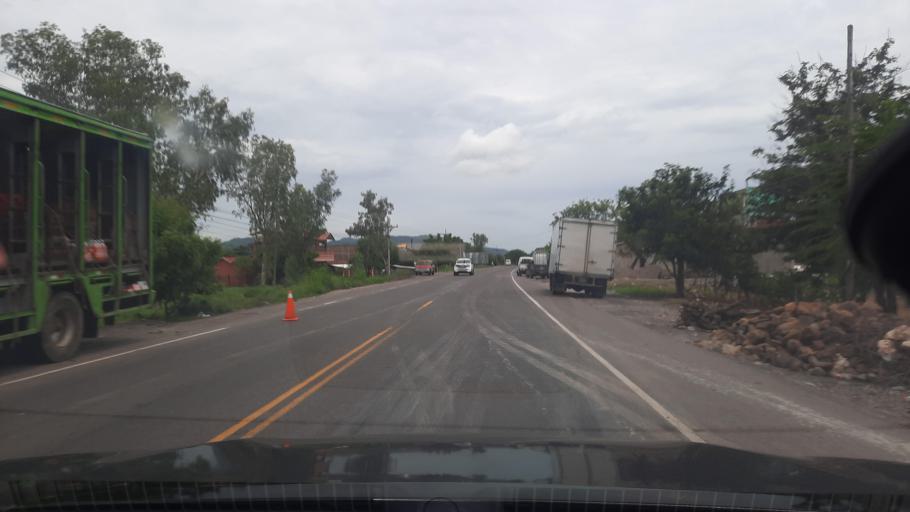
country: HN
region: Valle
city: Jicaro Galan
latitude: 13.5260
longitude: -87.4385
